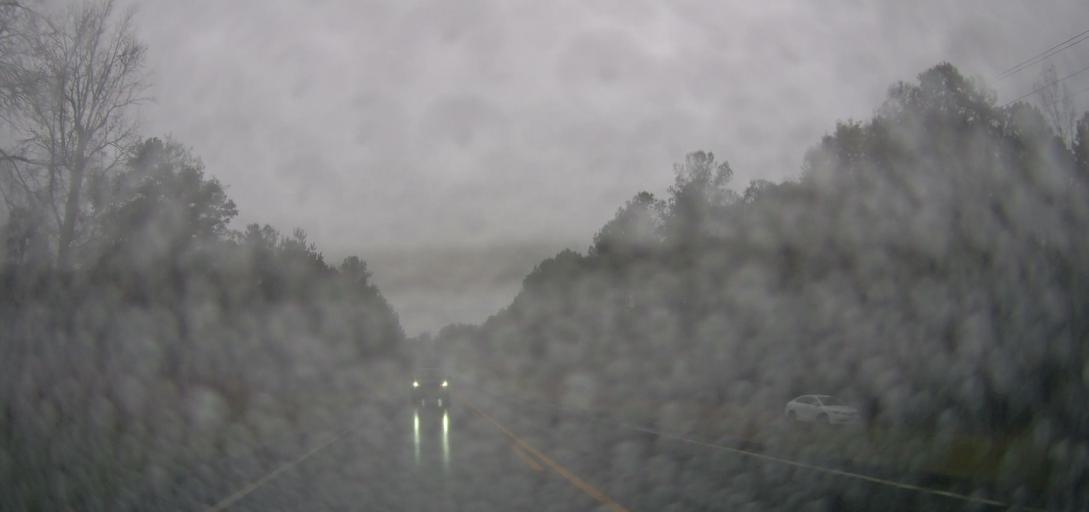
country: US
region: Georgia
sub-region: Putnam County
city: Eatonton
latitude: 33.2382
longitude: -83.4343
